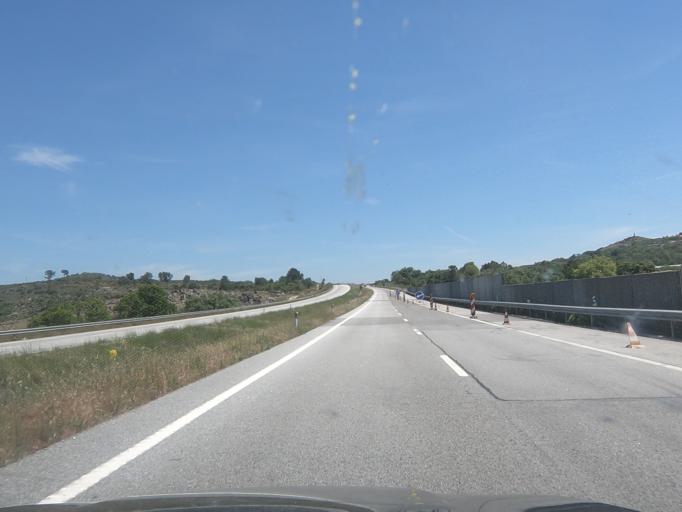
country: PT
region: Guarda
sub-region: Guarda
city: Sequeira
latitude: 40.5865
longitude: -7.1496
